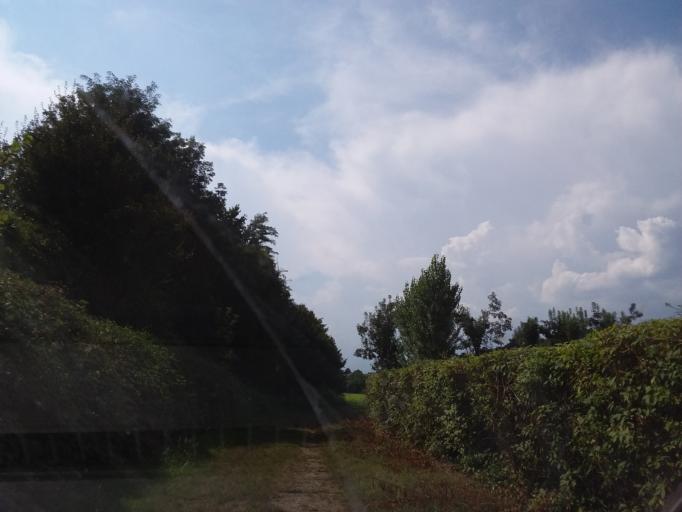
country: IT
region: Piedmont
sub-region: Provincia di Torino
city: Rivoli
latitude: 45.0742
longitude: 7.5347
